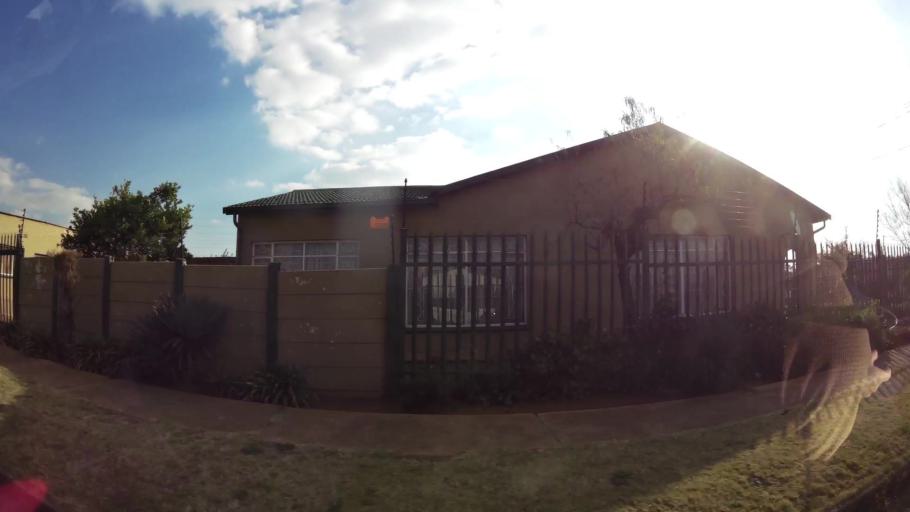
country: ZA
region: Gauteng
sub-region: West Rand District Municipality
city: Krugersdorp
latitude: -26.0918
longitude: 27.7455
